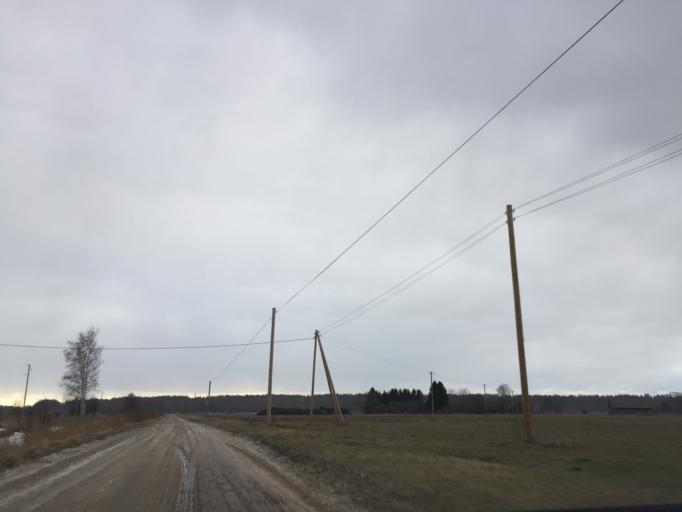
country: LV
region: Salacgrivas
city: Salacgriva
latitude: 57.6461
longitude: 24.3943
